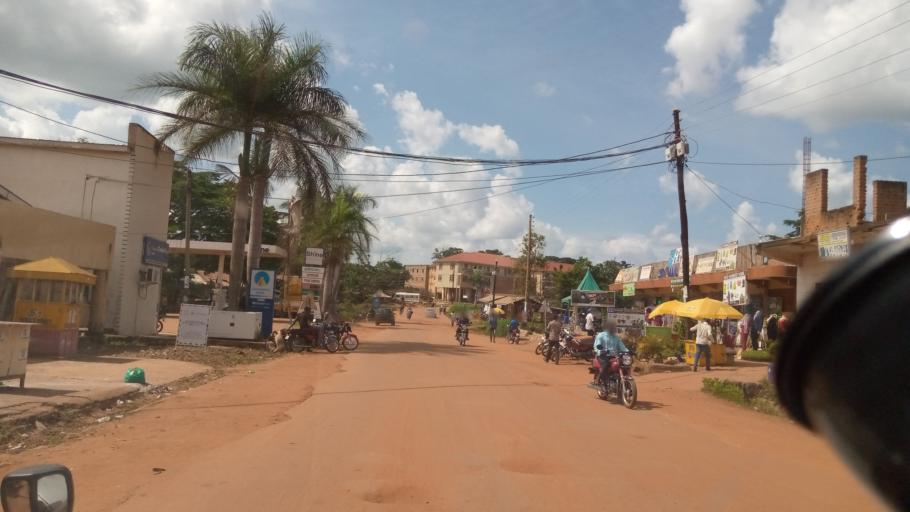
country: UG
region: Northern Region
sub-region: Lira District
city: Lira
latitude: 2.2458
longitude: 32.8970
